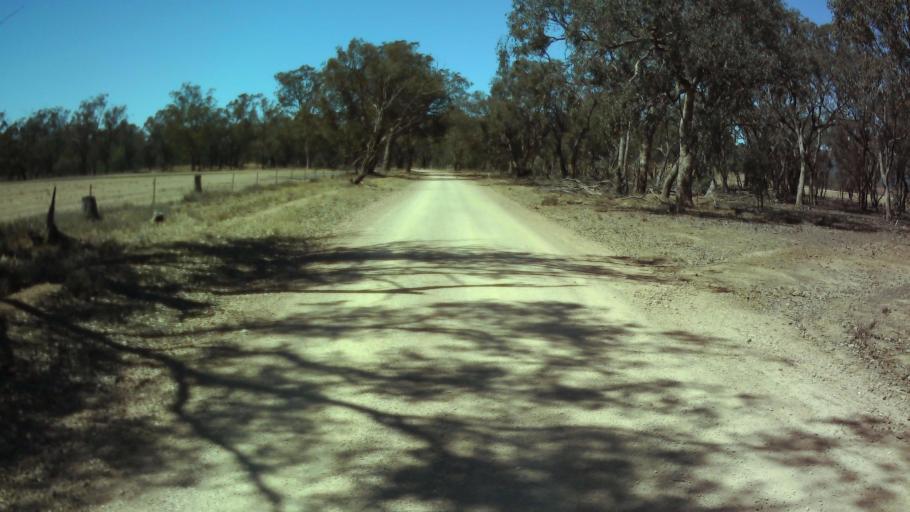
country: AU
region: New South Wales
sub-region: Weddin
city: Grenfell
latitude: -33.9355
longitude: 148.0774
